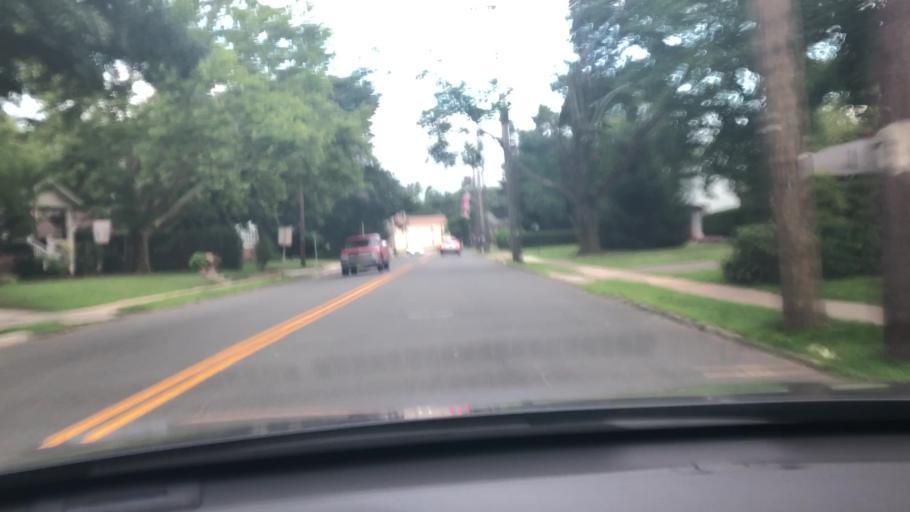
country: US
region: New Jersey
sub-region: Middlesex County
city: Milltown
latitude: 40.4590
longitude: -74.4462
